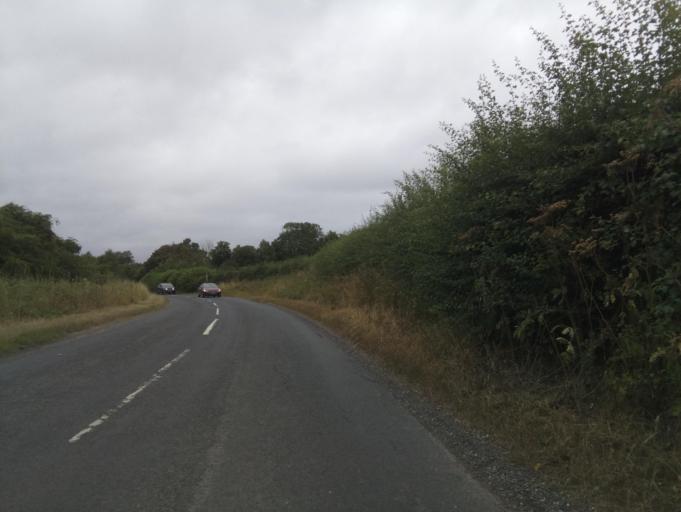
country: GB
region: England
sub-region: Derbyshire
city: Swadlincote
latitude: 52.7902
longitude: -1.5330
